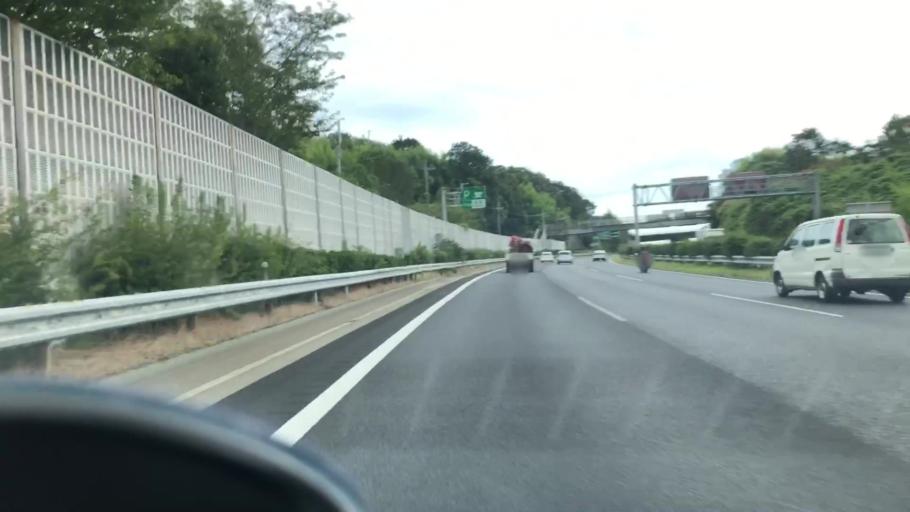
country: JP
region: Hyogo
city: Sandacho
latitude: 34.8912
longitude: 135.1588
